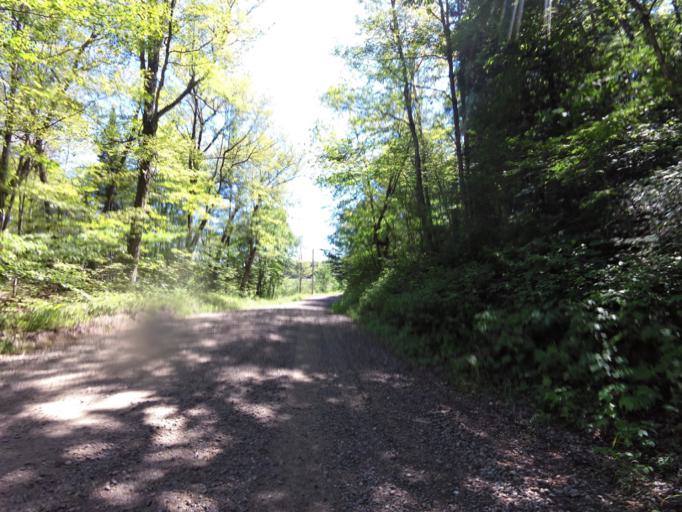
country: CA
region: Quebec
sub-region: Laurentides
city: Brownsburg-Chatham
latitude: 45.8285
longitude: -74.5287
